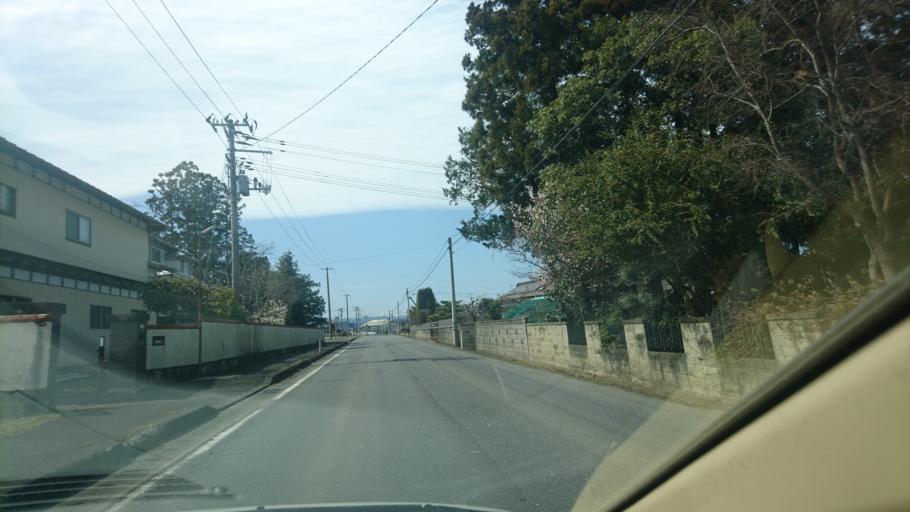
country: JP
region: Miyagi
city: Furukawa
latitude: 38.7410
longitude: 140.9628
